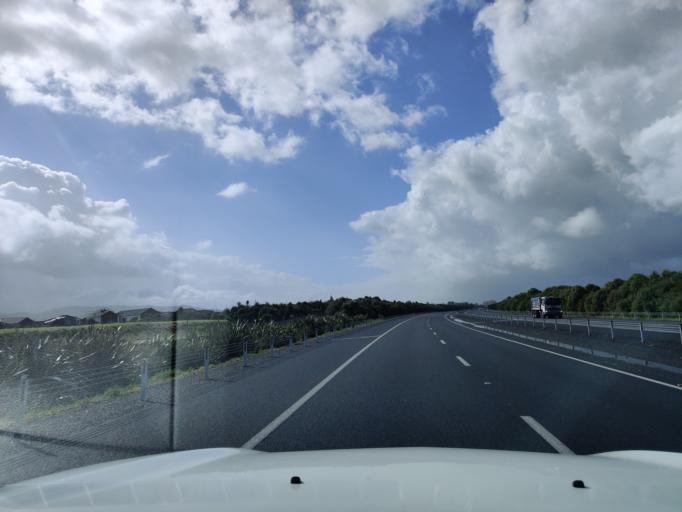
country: NZ
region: Waikato
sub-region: Waipa District
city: Cambridge
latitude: -37.8722
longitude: 175.4790
